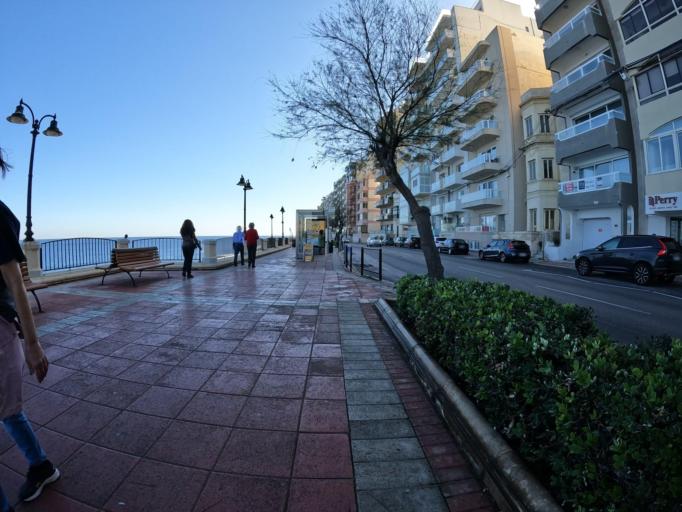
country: MT
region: Tas-Sliema
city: Sliema
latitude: 35.9172
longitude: 14.5007
